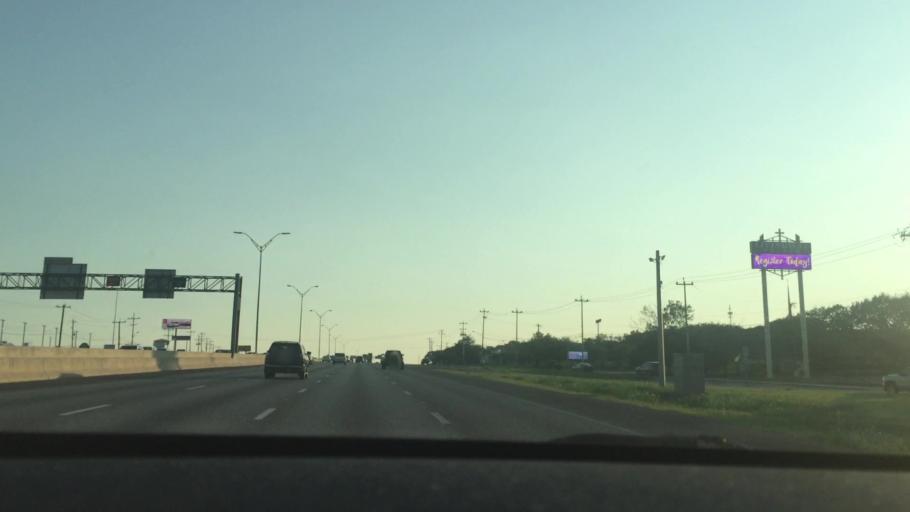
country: US
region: Texas
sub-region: Bexar County
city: Live Oak
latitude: 29.5597
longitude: -98.3428
